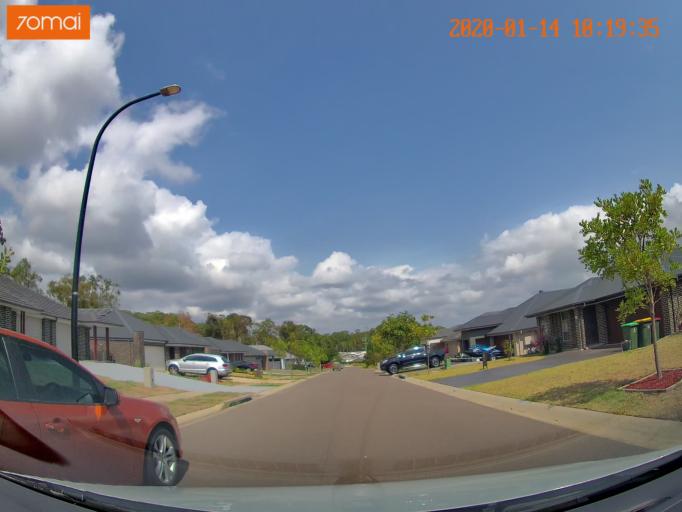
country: AU
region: New South Wales
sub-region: Lake Macquarie Shire
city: Dora Creek
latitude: -33.1098
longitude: 151.5060
